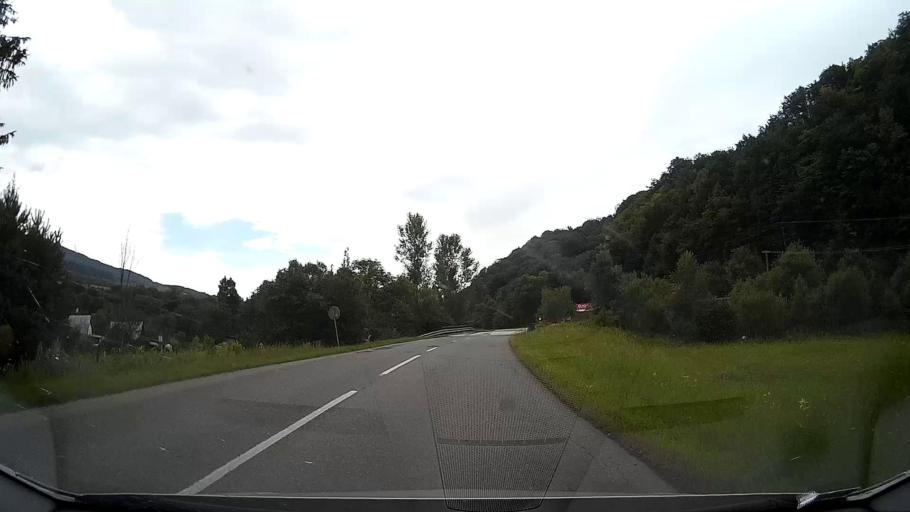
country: SK
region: Banskobystricky
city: Tisovec
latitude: 48.6620
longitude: 19.9418
